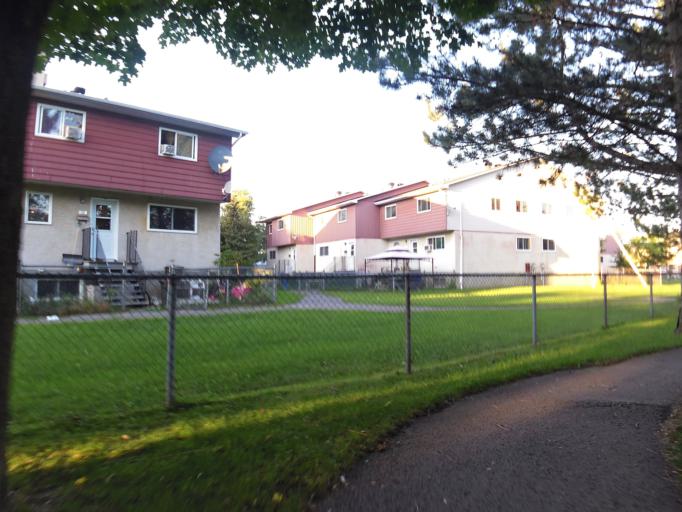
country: CA
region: Ontario
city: Ottawa
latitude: 45.4353
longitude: -75.7191
